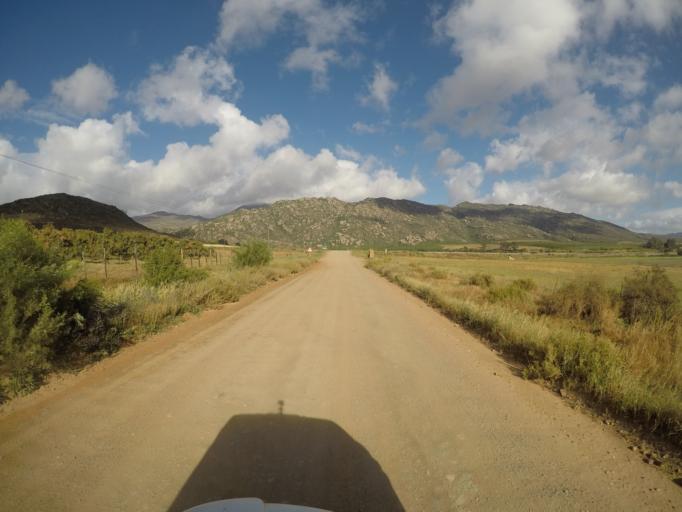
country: ZA
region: Western Cape
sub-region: West Coast District Municipality
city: Clanwilliam
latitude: -32.3636
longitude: 18.9414
